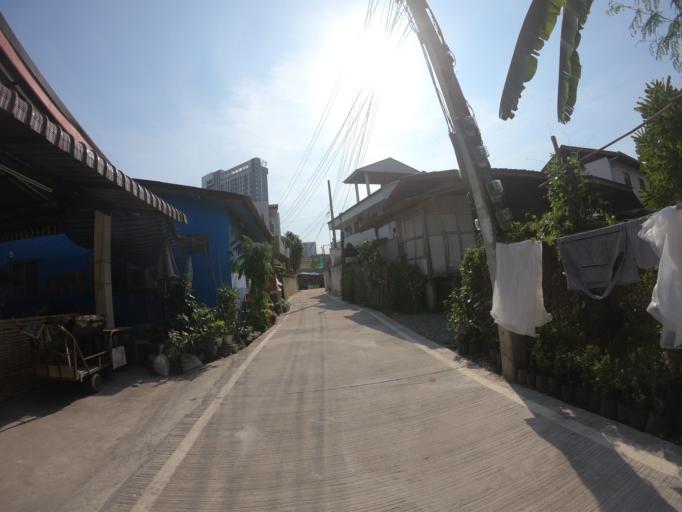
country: TH
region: Chiang Mai
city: Chiang Mai
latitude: 18.8076
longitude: 99.0202
